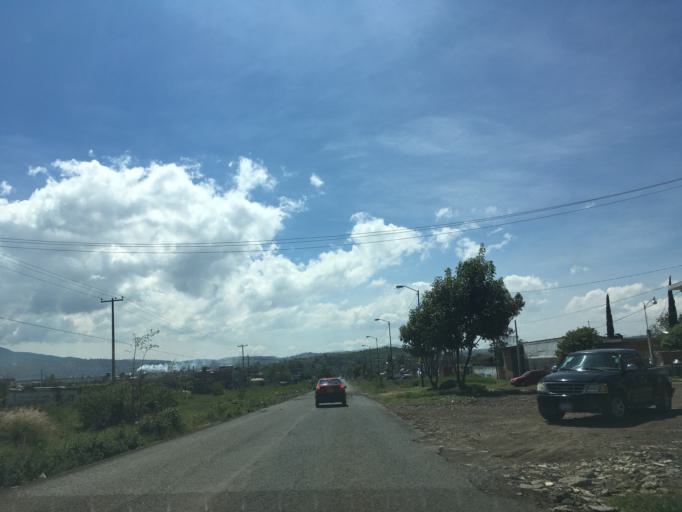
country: MX
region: Michoacan
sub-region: Morelia
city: San Antonio
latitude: 19.6843
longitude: -101.2793
